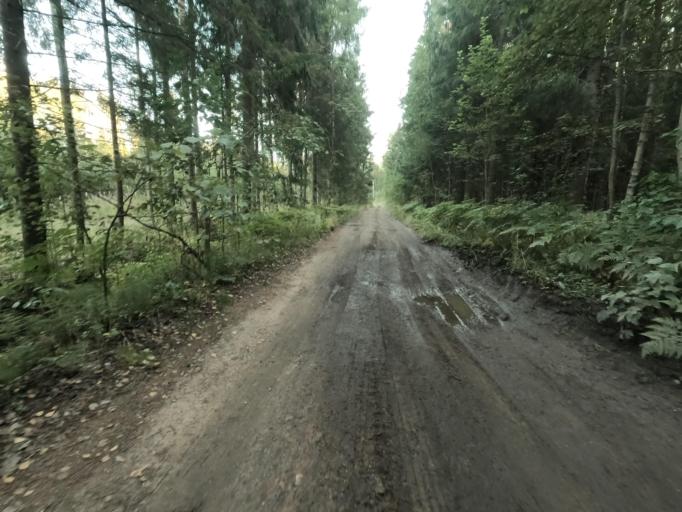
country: RU
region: Leningrad
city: Otradnoye
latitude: 59.8298
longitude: 30.7705
